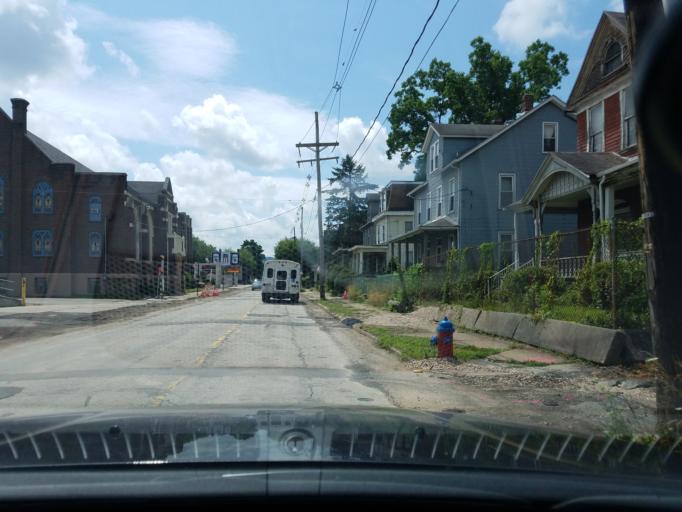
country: US
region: Pennsylvania
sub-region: Cambria County
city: Johnstown
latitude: 40.3202
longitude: -78.9194
